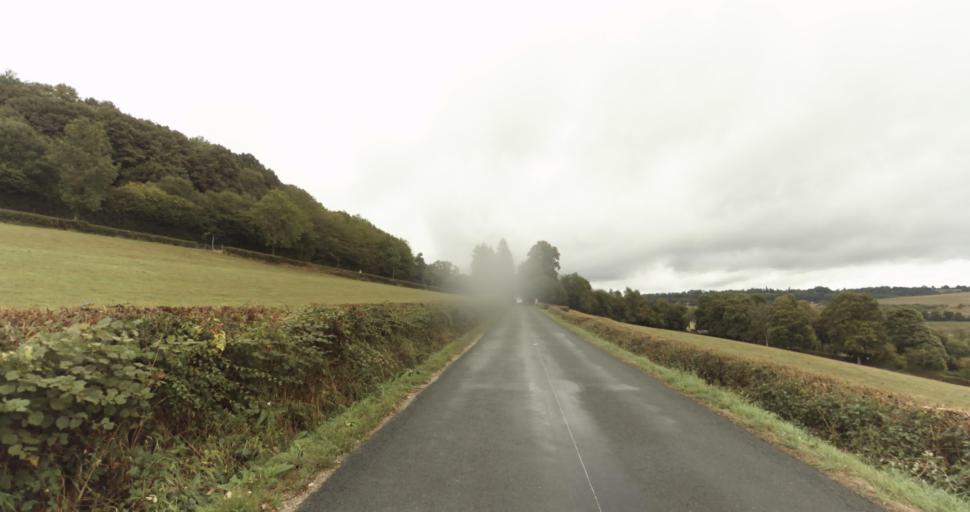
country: FR
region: Lower Normandy
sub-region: Departement de l'Orne
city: Vimoutiers
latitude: 48.9023
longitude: 0.2082
